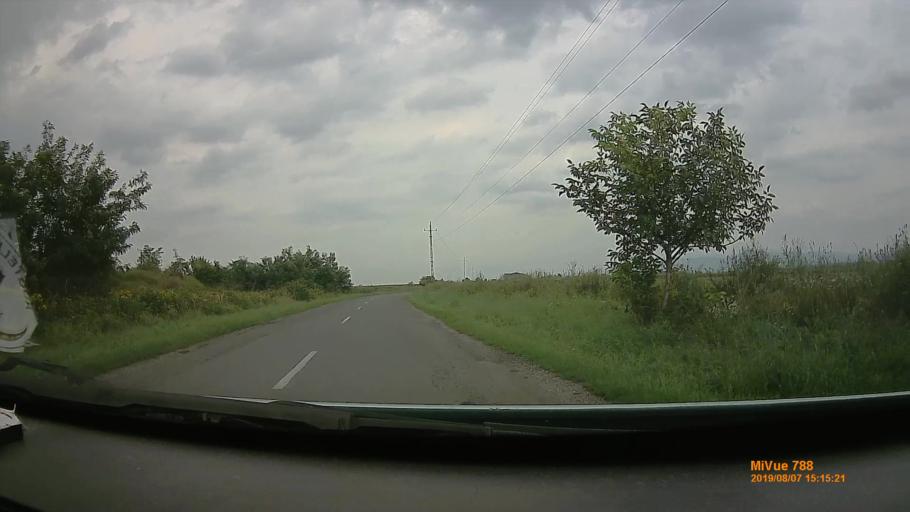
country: HU
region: Borsod-Abauj-Zemplen
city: Encs
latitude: 48.3379
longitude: 21.1290
